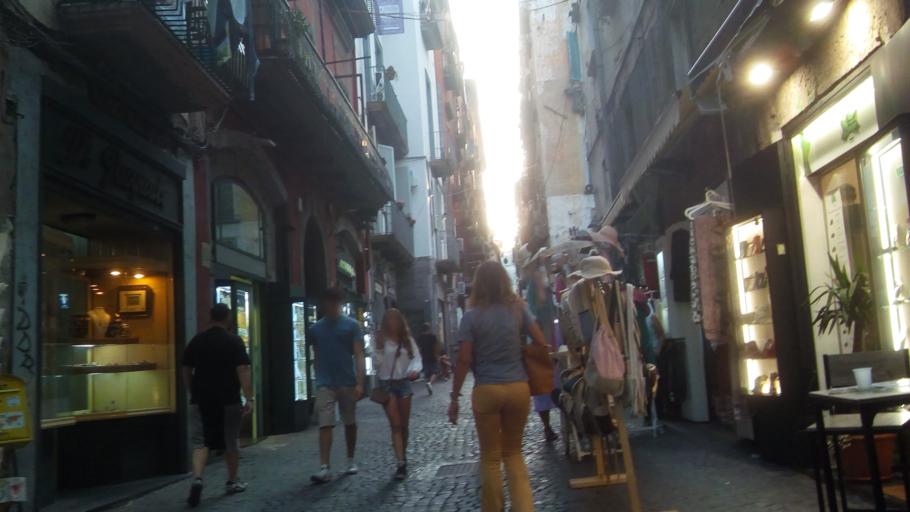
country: IT
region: Campania
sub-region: Provincia di Napoli
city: Napoli
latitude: 40.8492
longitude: 14.2587
